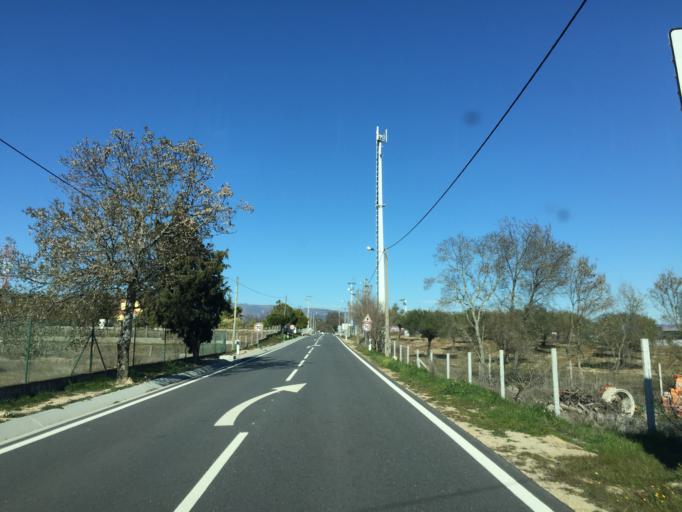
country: PT
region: Guarda
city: Alcains
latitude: 39.9808
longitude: -7.4572
